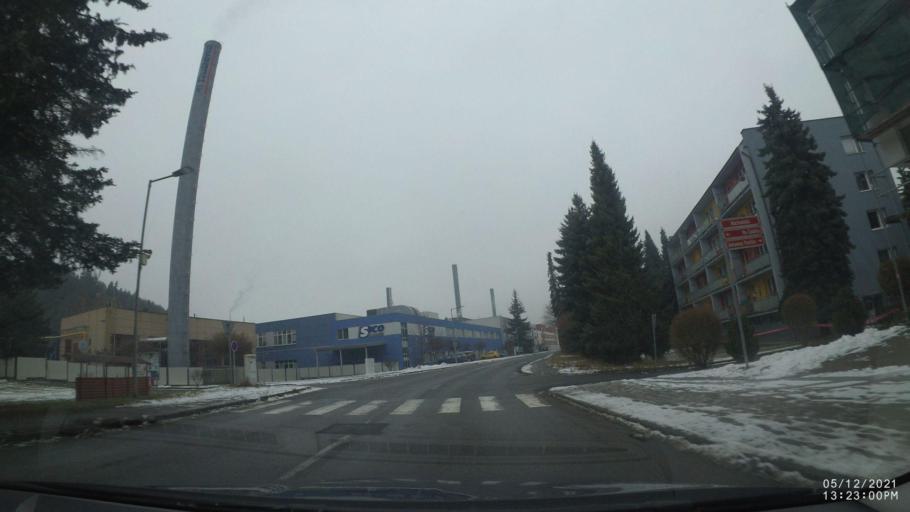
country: CZ
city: Velke Porici
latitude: 50.4685
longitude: 16.1806
